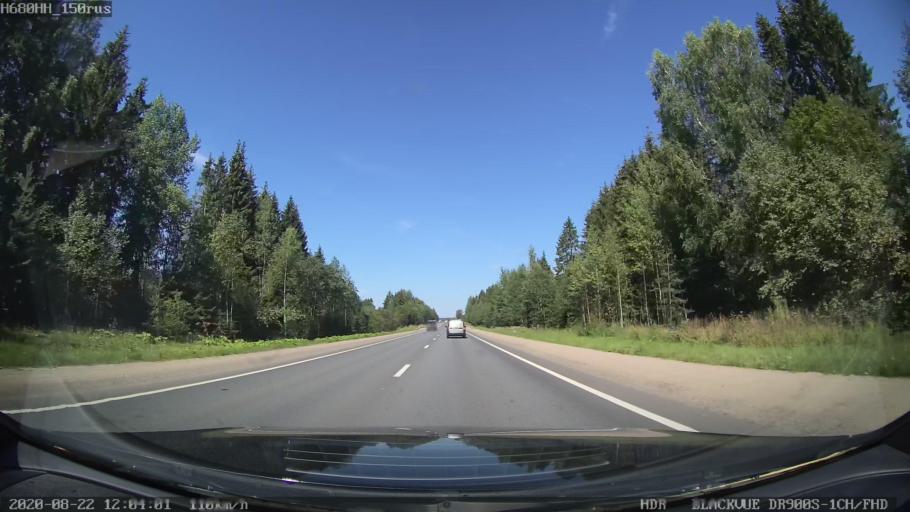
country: RU
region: Tverskaya
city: Rameshki
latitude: 57.2628
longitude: 36.0779
